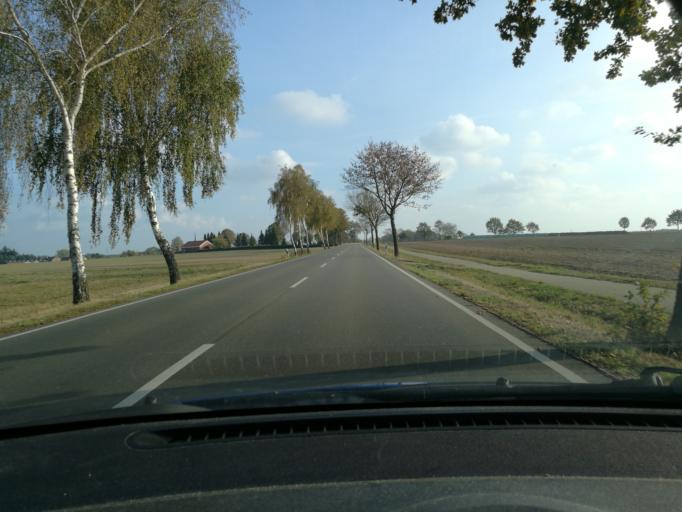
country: DE
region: Lower Saxony
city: Luechow
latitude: 52.9871
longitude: 11.1229
